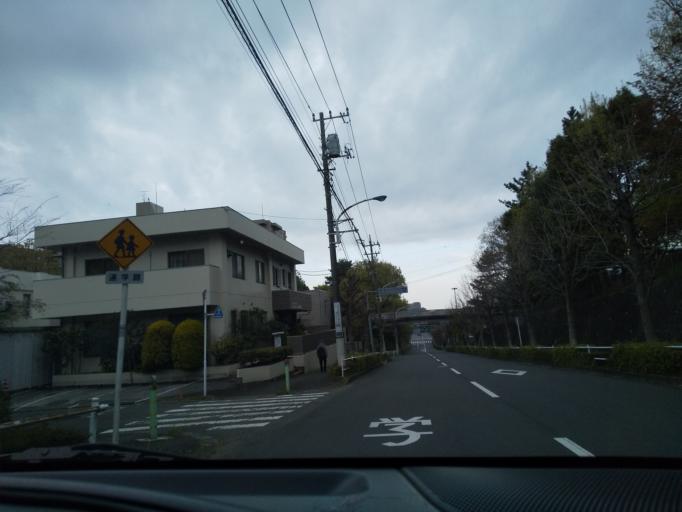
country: JP
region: Tokyo
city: Hino
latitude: 35.6087
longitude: 139.3822
